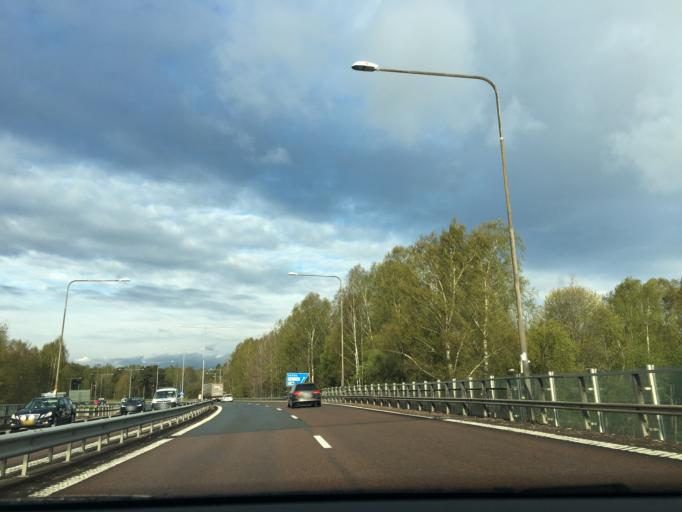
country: SE
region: Vaermland
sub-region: Karlstads Kommun
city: Karlstad
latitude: 59.3980
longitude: 13.5039
